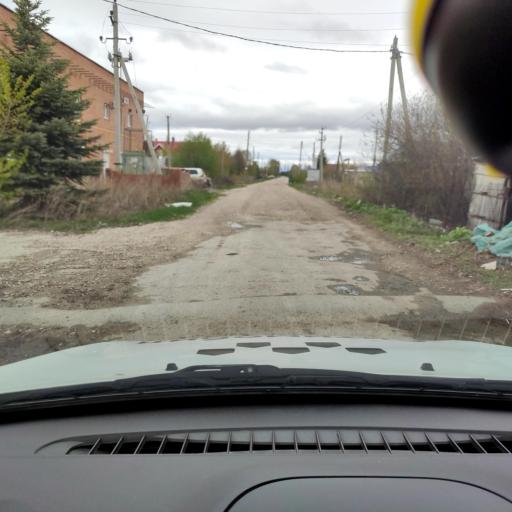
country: RU
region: Samara
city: Tol'yatti
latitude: 53.5774
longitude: 49.3290
